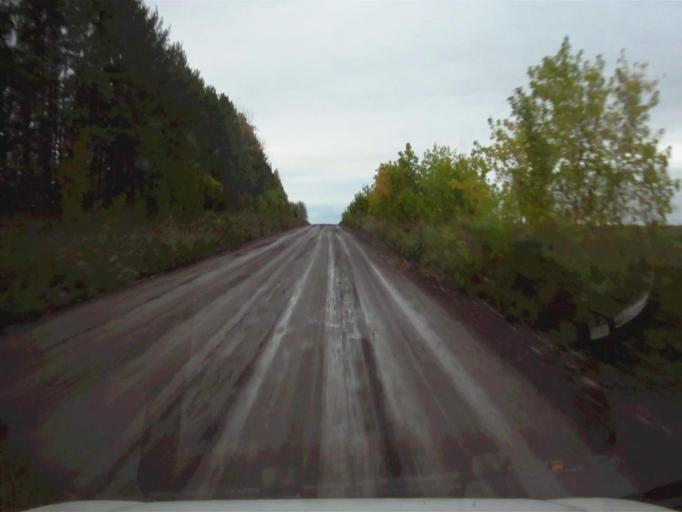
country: RU
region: Sverdlovsk
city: Mikhaylovsk
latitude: 56.1551
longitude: 59.2607
